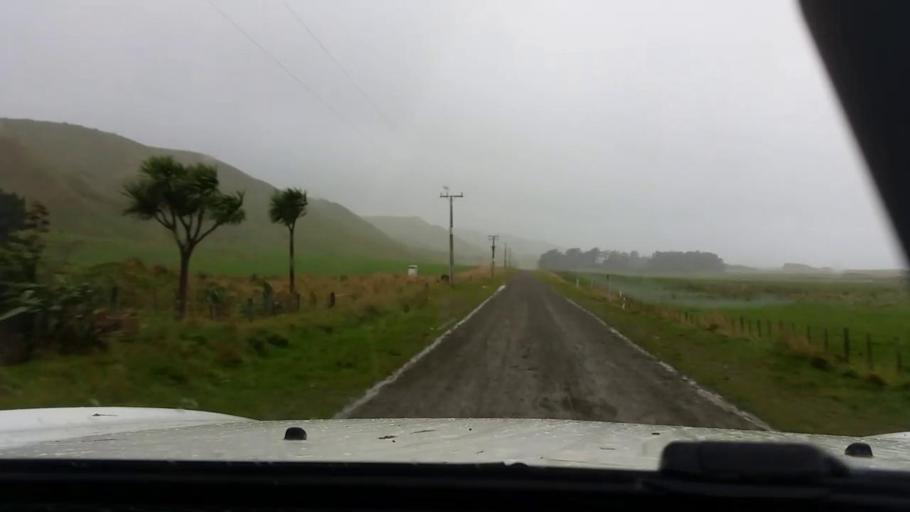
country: NZ
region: Wellington
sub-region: Masterton District
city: Masterton
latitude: -41.2568
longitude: 175.9049
